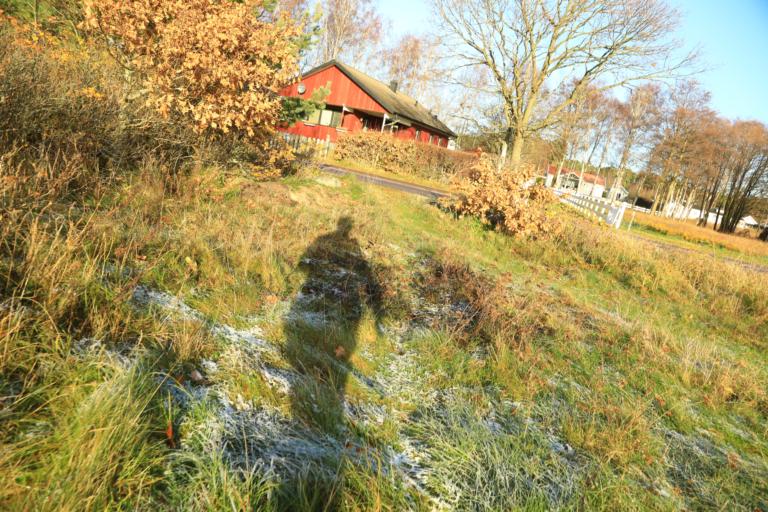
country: SE
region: Halland
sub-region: Varbergs Kommun
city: Varberg
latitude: 57.1910
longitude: 12.1867
